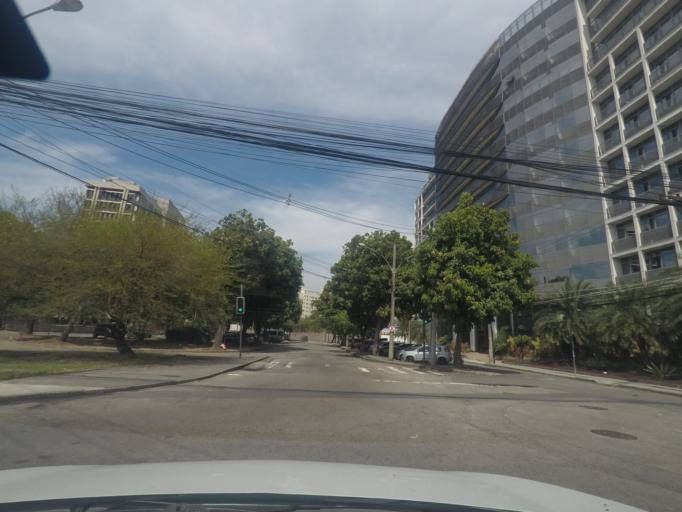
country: BR
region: Rio de Janeiro
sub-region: Rio De Janeiro
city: Rio de Janeiro
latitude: -22.9072
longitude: -43.2179
